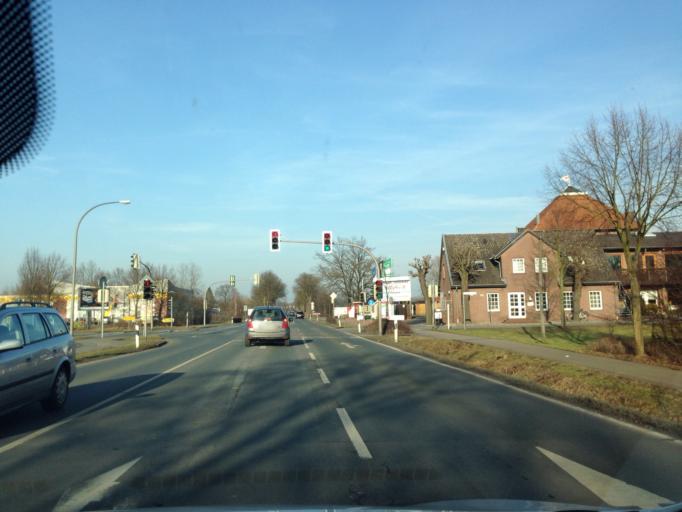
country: DE
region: North Rhine-Westphalia
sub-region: Regierungsbezirk Munster
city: Muenster
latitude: 51.9926
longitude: 7.6657
